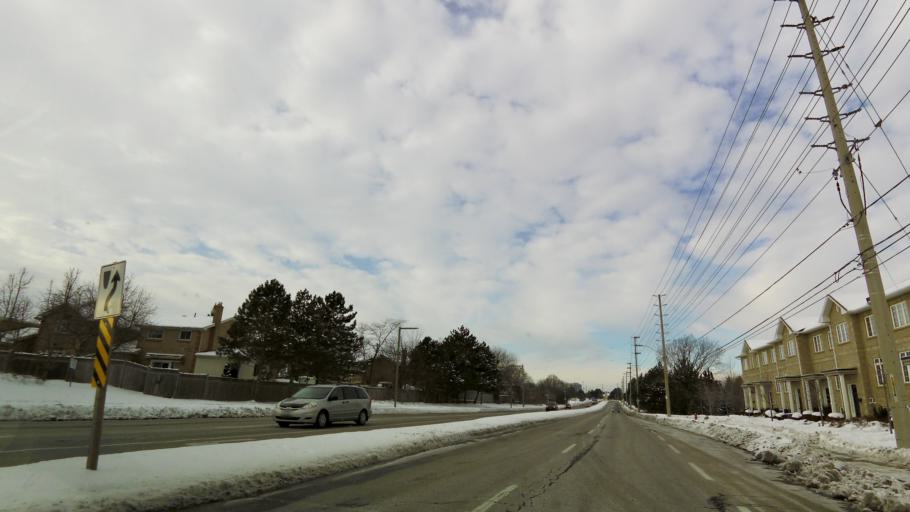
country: CA
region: Ontario
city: Mississauga
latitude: 43.5435
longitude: -79.6919
